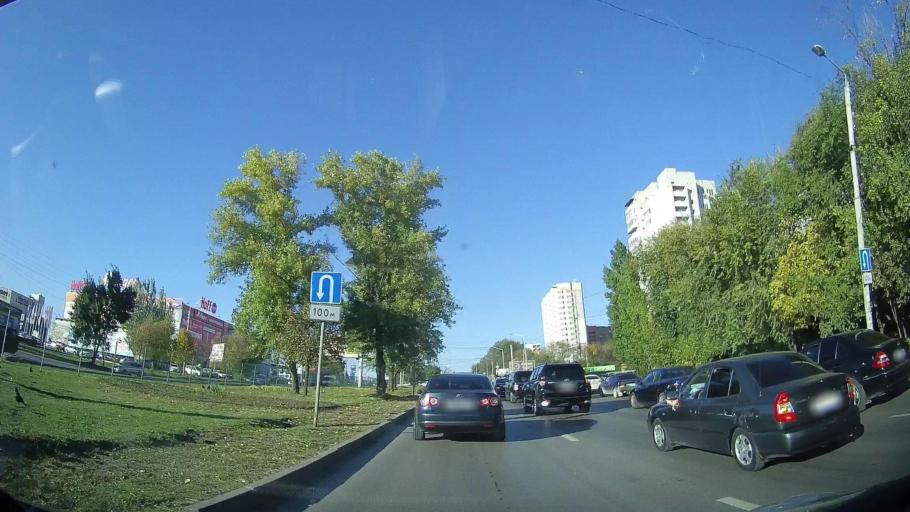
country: RU
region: Rostov
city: Kalinin
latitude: 47.2301
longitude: 39.6140
